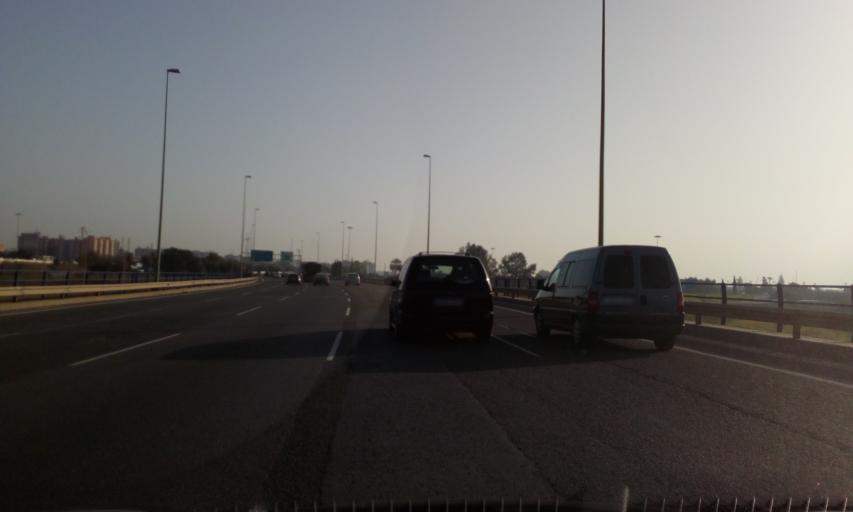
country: ES
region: Andalusia
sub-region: Provincia de Sevilla
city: San Juan de Aznalfarache
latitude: 37.3713
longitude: -6.0200
